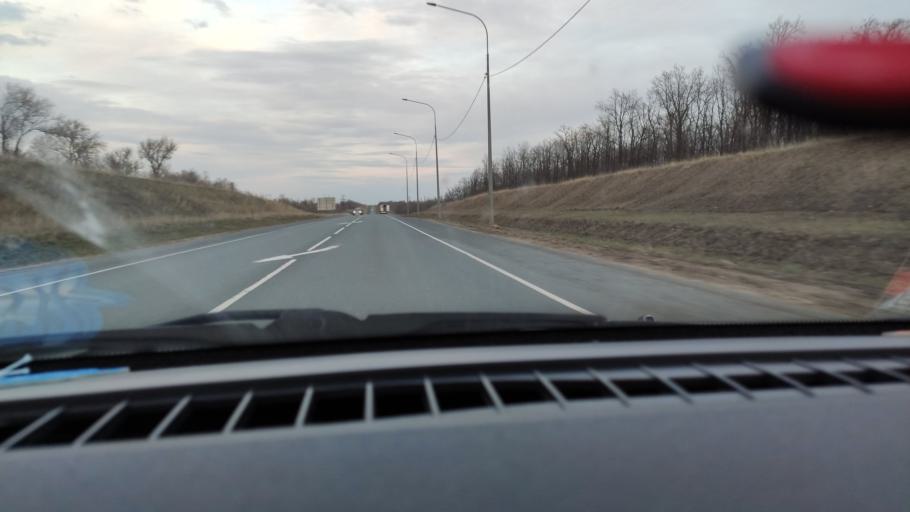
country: RU
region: Saratov
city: Yelshanka
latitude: 51.8225
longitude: 46.3236
